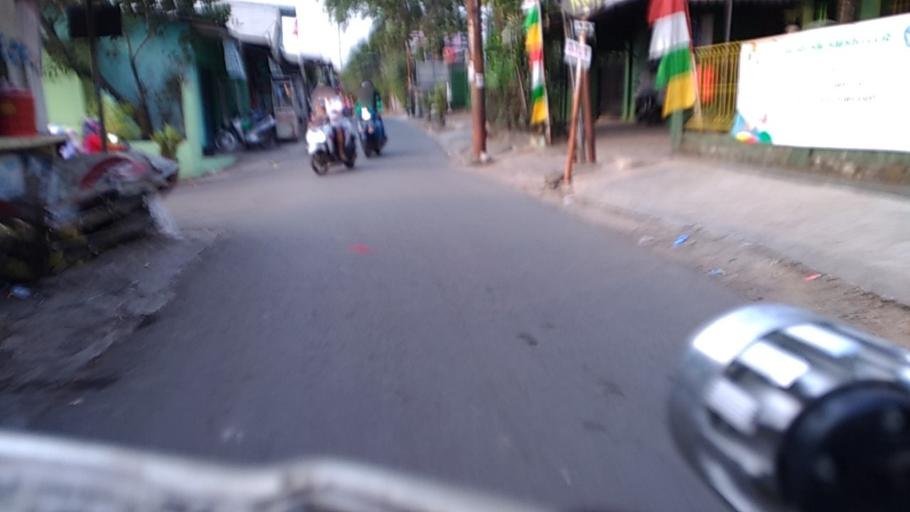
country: ID
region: West Java
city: Depok
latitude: -6.3577
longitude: 106.8796
